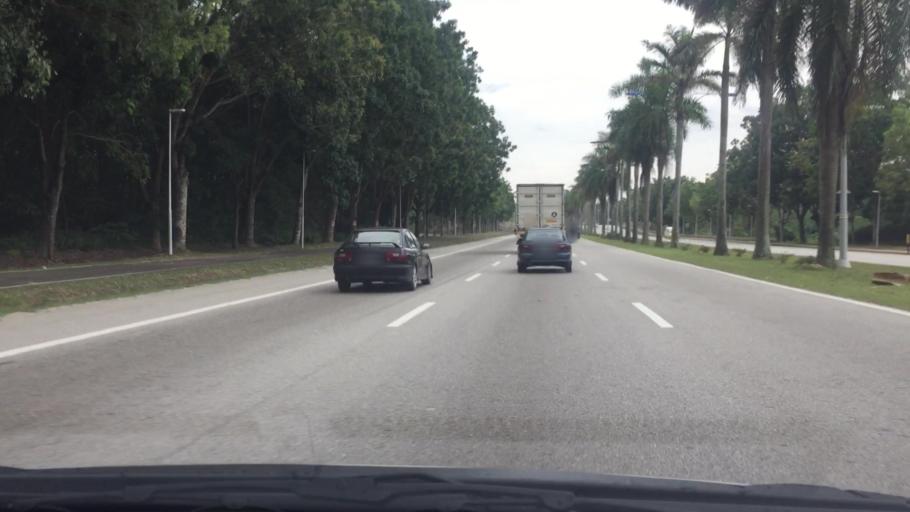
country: MY
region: Putrajaya
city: Putrajaya
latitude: 2.9030
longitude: 101.6582
